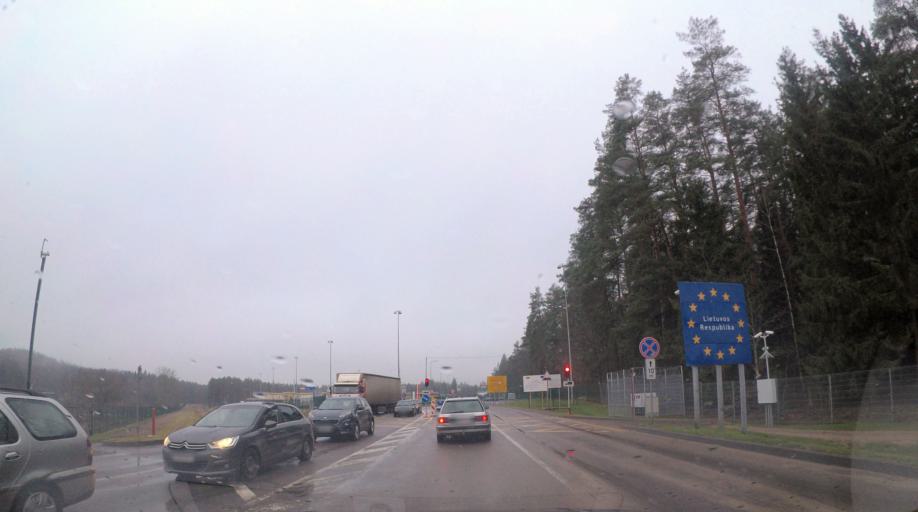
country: BY
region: Grodnenskaya
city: Astravyets
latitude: 54.7189
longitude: 25.7455
